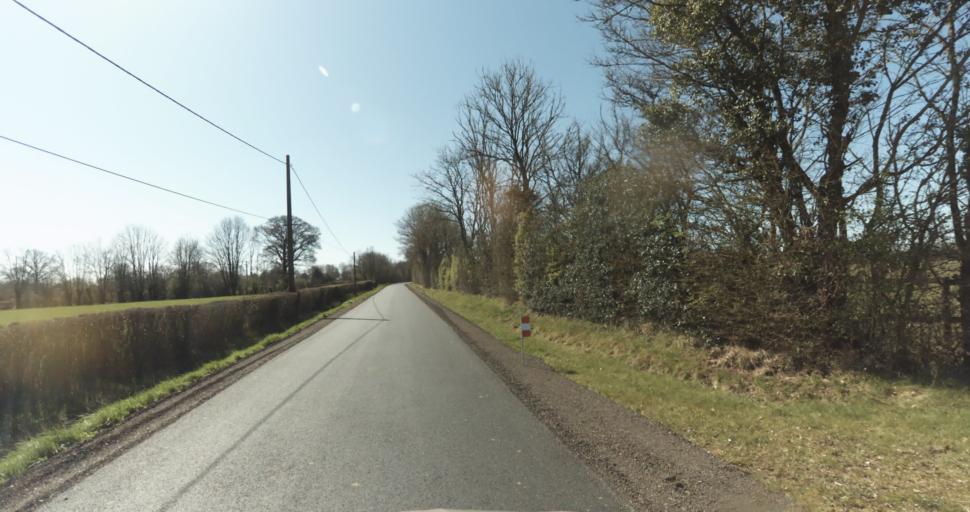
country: FR
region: Lower Normandy
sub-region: Departement du Calvados
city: Livarot
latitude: 48.9439
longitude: 0.0843
